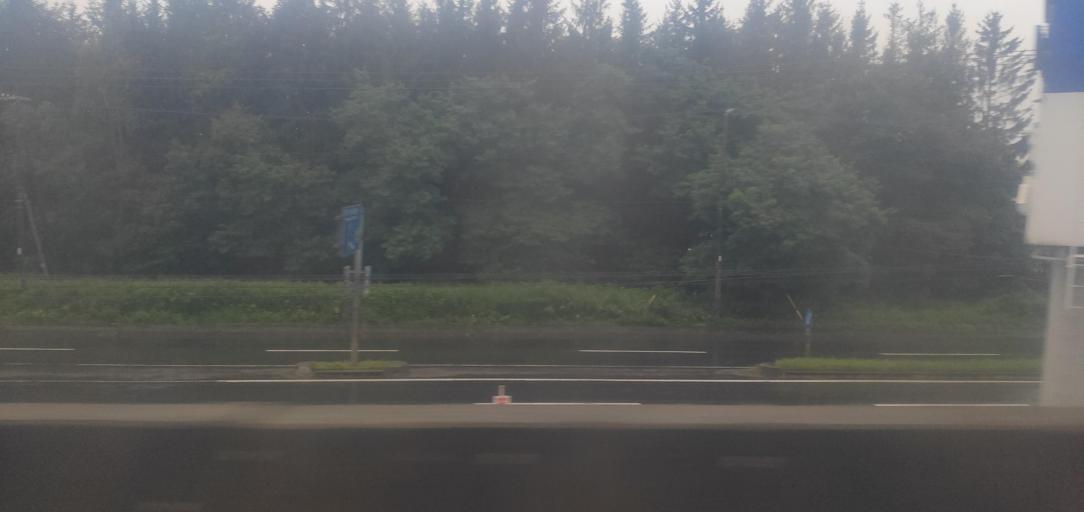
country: JP
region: Hokkaido
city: Chitose
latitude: 42.8199
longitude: 141.6613
